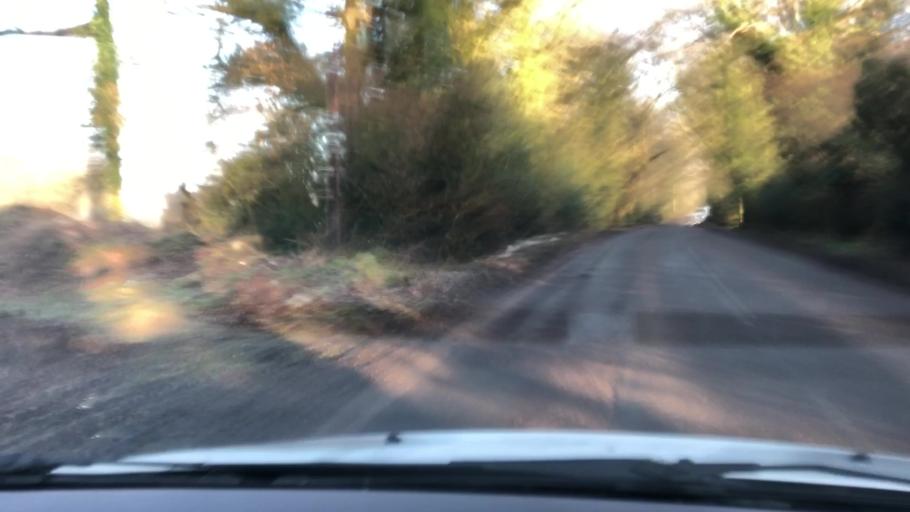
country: GB
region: England
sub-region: Hampshire
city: Alton
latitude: 51.1875
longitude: -1.0023
